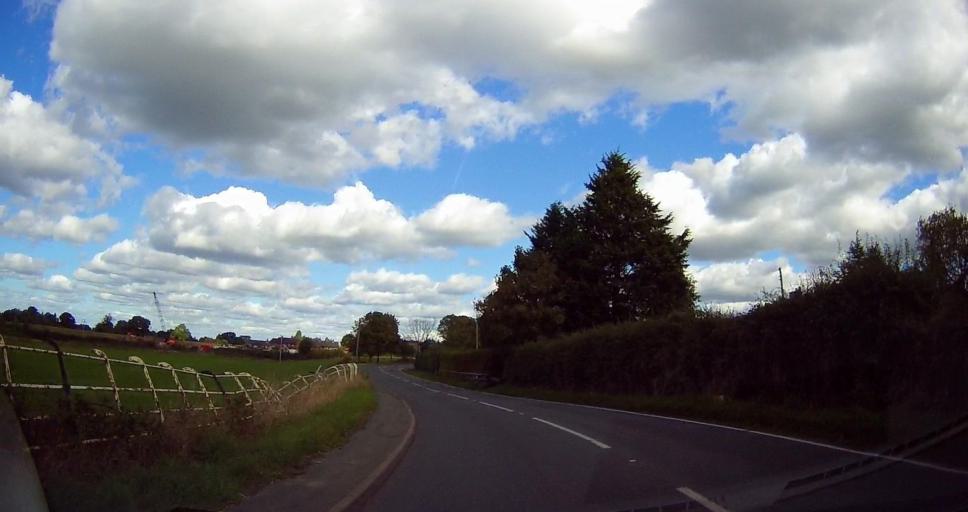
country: GB
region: England
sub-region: Shropshire
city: Market Drayton
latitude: 52.9850
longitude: -2.4740
